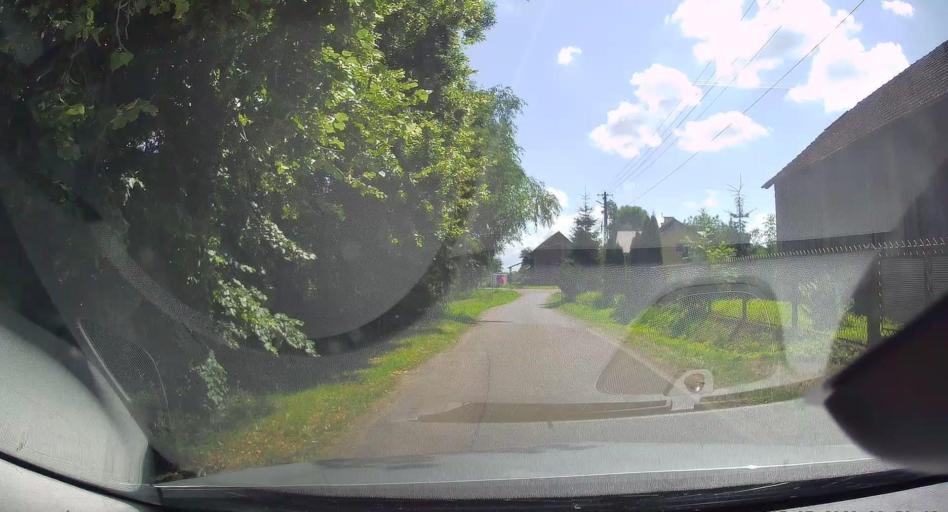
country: PL
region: Subcarpathian Voivodeship
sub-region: Powiat jaroslawski
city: Sosnica
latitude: 49.8626
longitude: 22.8806
